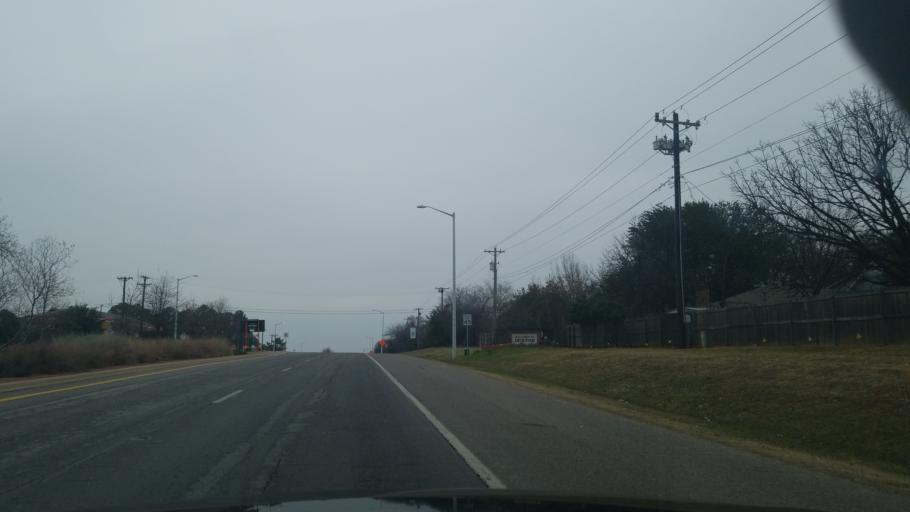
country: US
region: Texas
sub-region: Denton County
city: Denton
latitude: 33.1936
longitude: -97.1167
